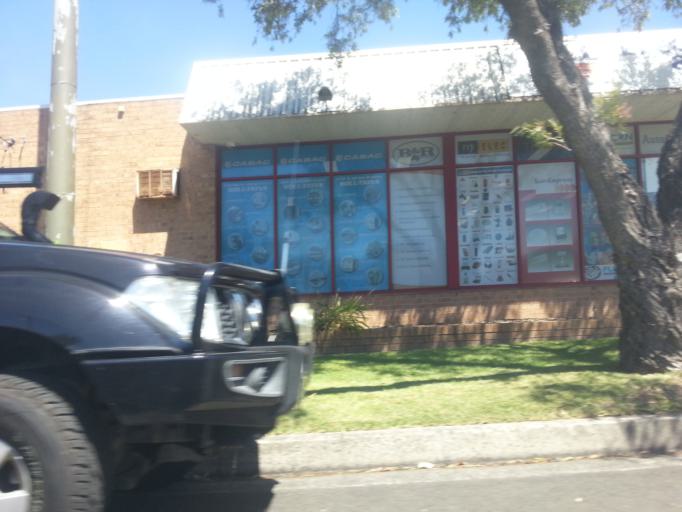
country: AU
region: New South Wales
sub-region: Wollongong
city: Wollongong
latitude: -34.4305
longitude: 150.8914
